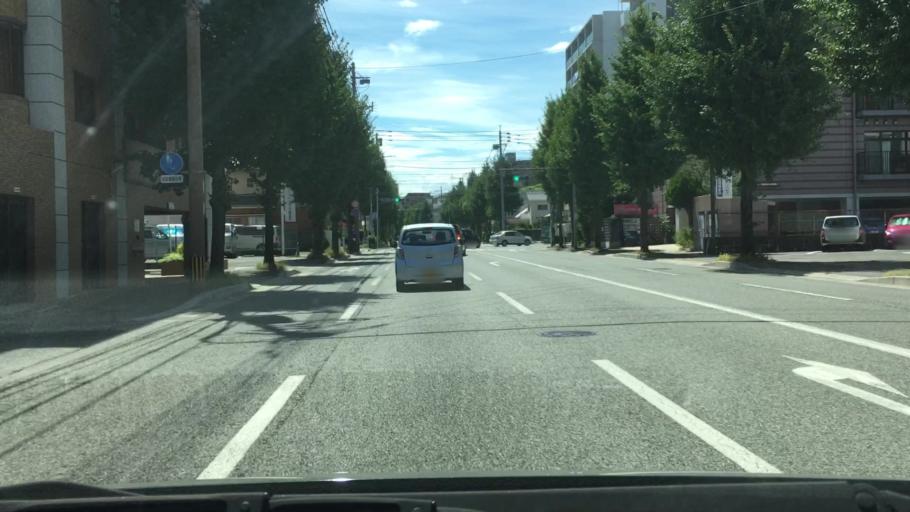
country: JP
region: Fukuoka
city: Fukuoka-shi
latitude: 33.5668
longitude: 130.4274
